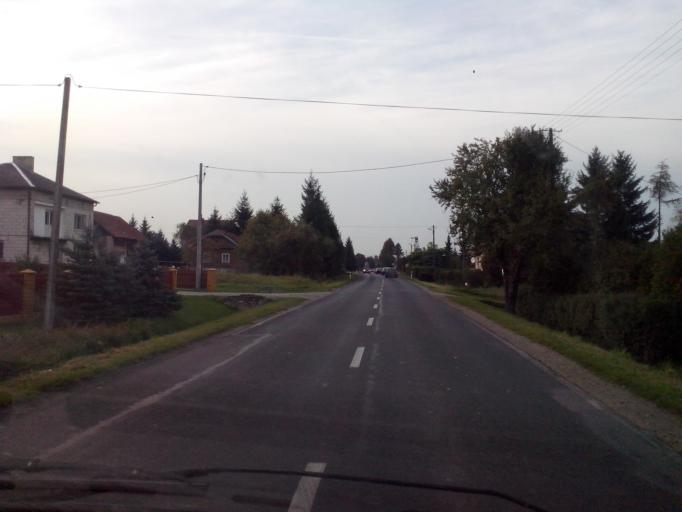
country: PL
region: Subcarpathian Voivodeship
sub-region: Powiat strzyzowski
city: Strzyzow
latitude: 49.8393
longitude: 21.8215
